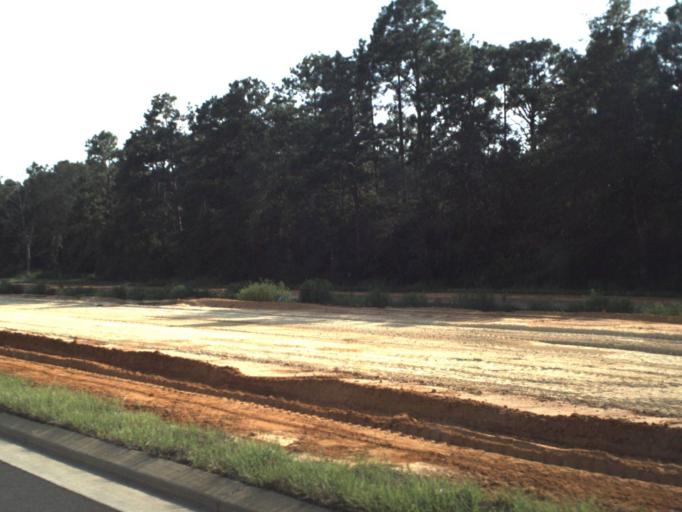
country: US
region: Florida
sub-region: Walton County
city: DeFuniak Springs
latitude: 30.6486
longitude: -86.1135
